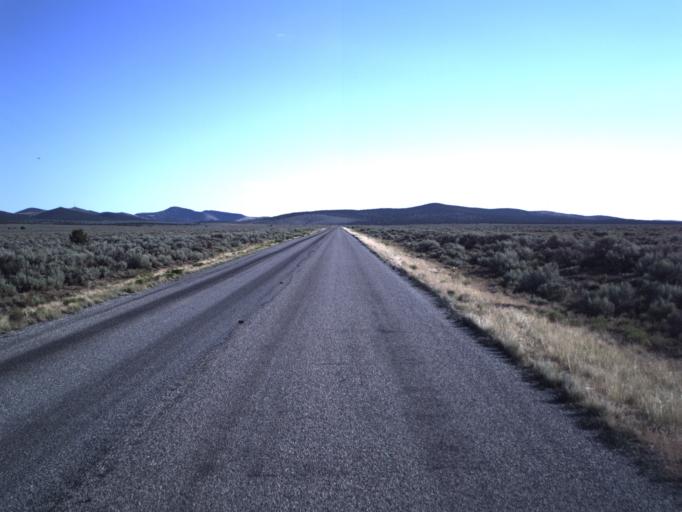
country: US
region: Utah
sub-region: Iron County
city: Enoch
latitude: 37.9880
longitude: -113.0015
